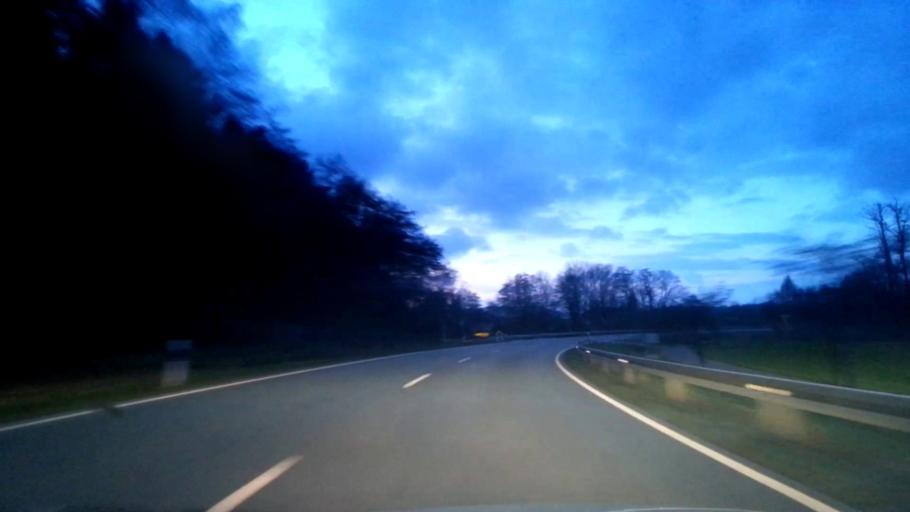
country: DE
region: Bavaria
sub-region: Upper Franconia
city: Kirchenpingarten
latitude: 49.9362
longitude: 11.7403
